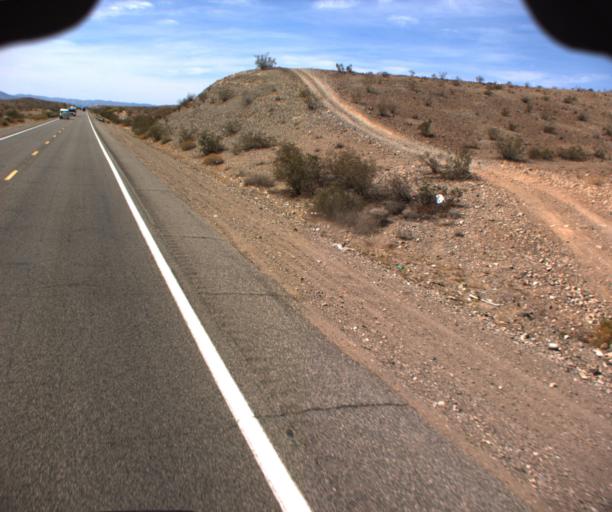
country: US
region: Arizona
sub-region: Mohave County
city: Lake Havasu City
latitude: 34.4348
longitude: -114.2205
